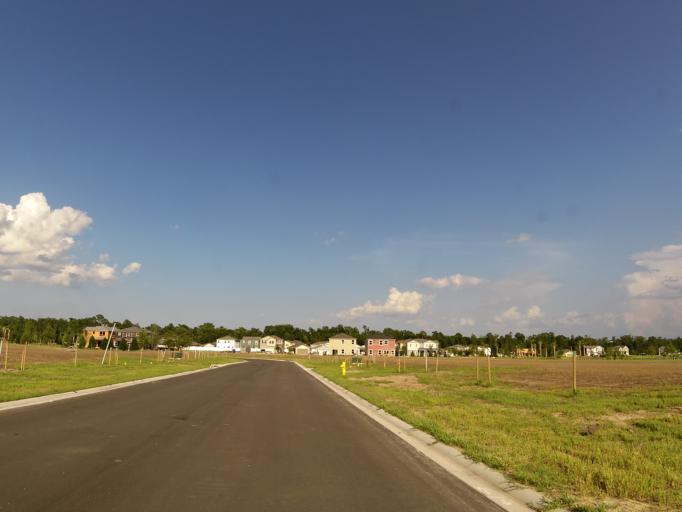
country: US
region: Florida
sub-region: Clay County
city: Green Cove Springs
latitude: 30.0313
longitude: -81.6331
